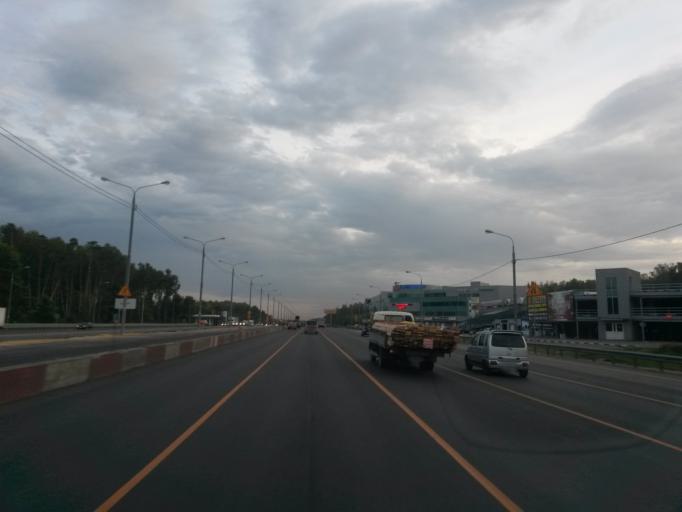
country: RU
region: Moskovskaya
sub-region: Podol'skiy Rayon
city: Podol'sk
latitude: 55.4184
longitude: 37.6097
